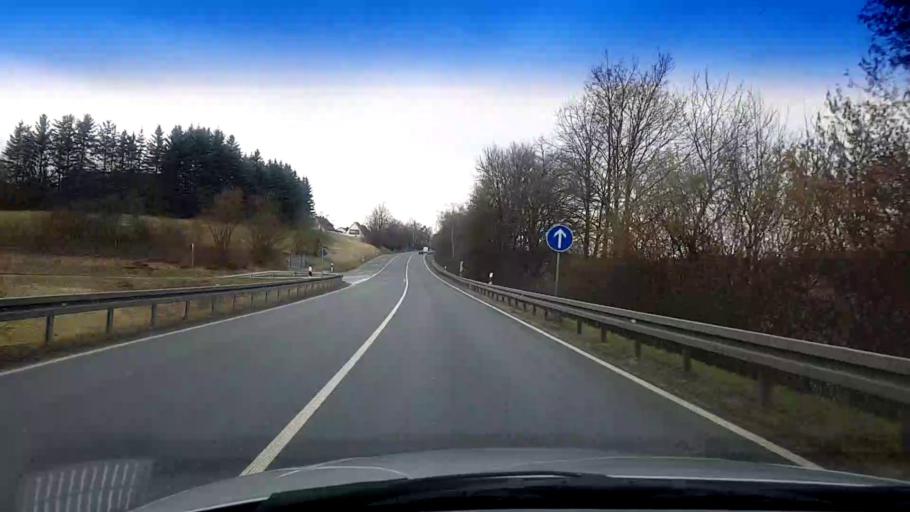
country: DE
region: Bavaria
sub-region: Upper Franconia
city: Kulmbach
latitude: 50.0787
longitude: 11.4669
